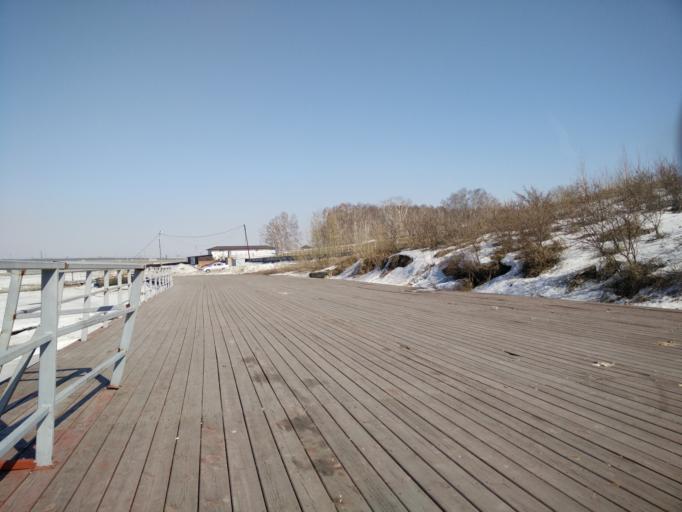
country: RU
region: Novosibirsk
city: Berdsk
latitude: 54.7743
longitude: 83.0813
